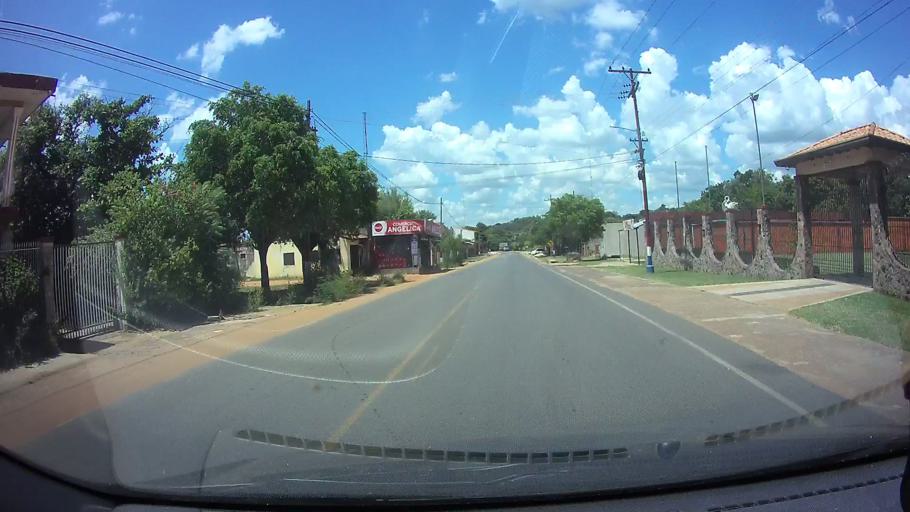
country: PY
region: Central
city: Limpio
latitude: -25.1811
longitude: -57.4470
